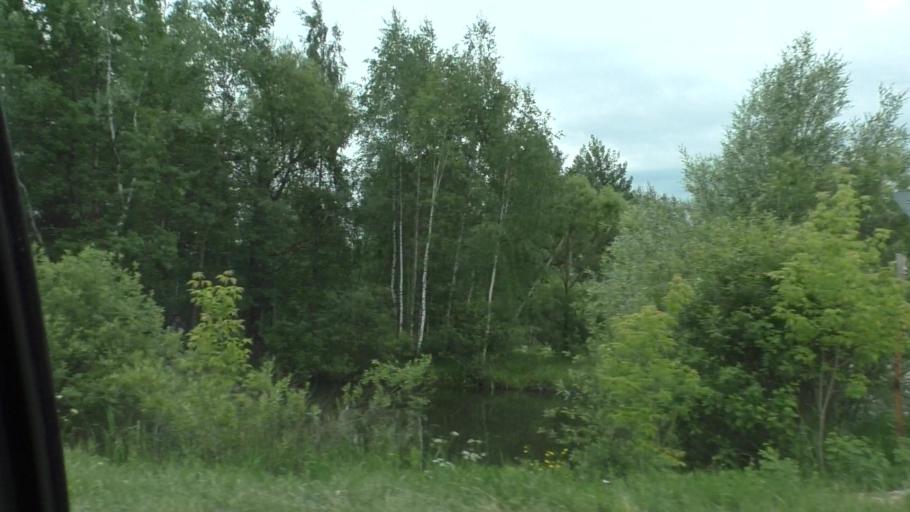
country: RU
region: Moskovskaya
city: Il'inskiy Pogost
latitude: 55.4687
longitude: 38.8977
